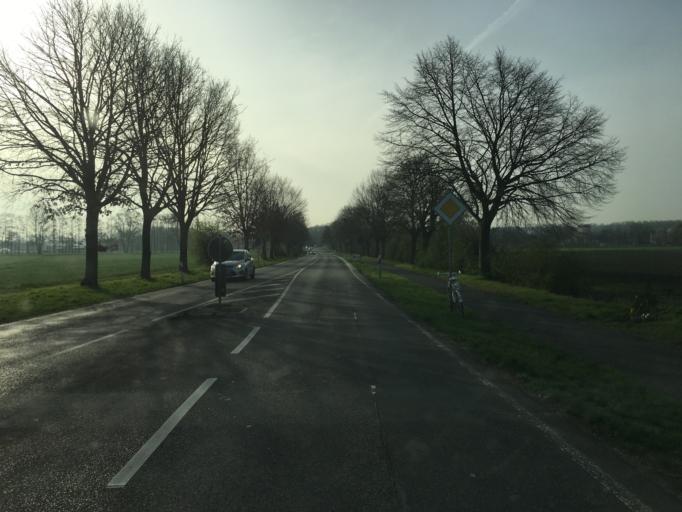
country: DE
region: North Rhine-Westphalia
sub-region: Regierungsbezirk Koln
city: Hurth
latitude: 50.8913
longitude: 6.8542
